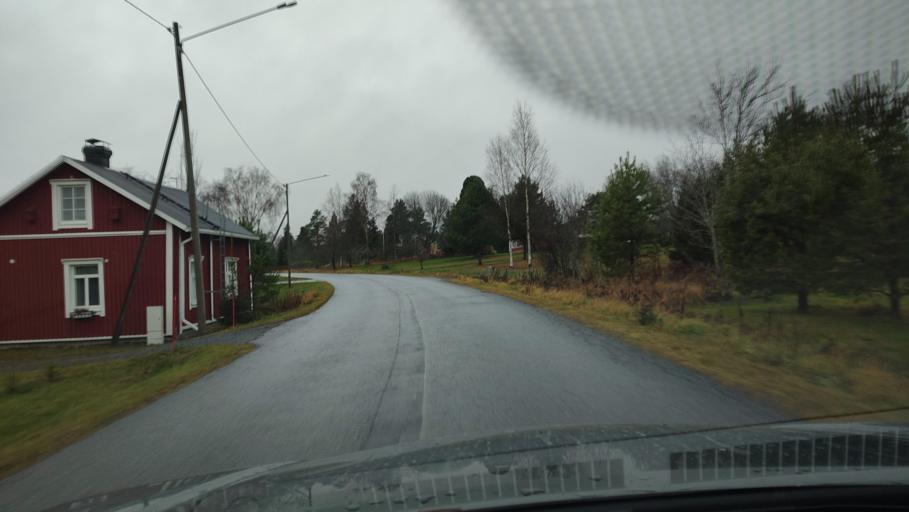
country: FI
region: Ostrobothnia
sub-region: Sydosterbotten
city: Kristinestad
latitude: 62.2644
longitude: 21.4746
